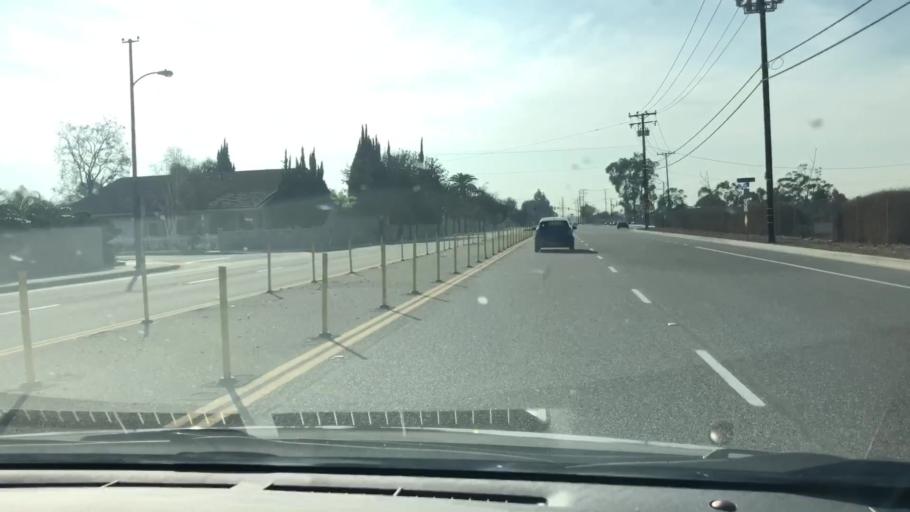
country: US
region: California
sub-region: Orange County
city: Villa Park
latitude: 33.8128
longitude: -117.7924
